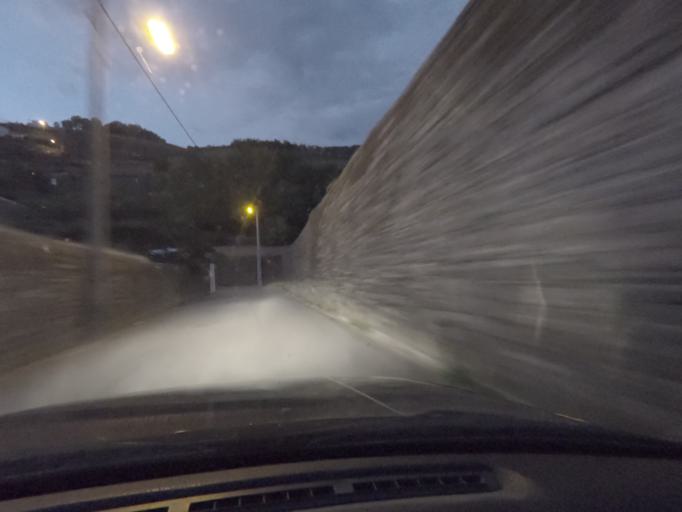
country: PT
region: Vila Real
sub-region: Peso da Regua
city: Godim
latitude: 41.1760
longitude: -7.8295
